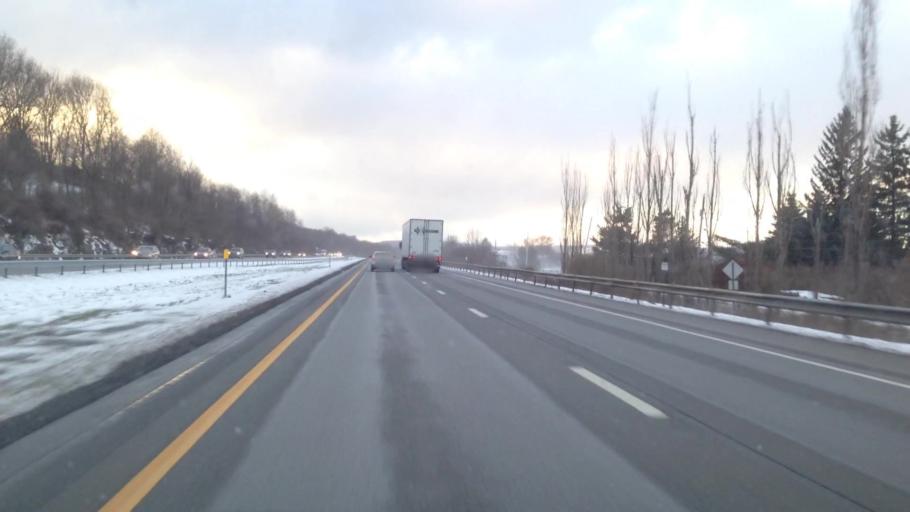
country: US
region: New York
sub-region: Herkimer County
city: Little Falls
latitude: 43.0060
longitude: -74.8938
